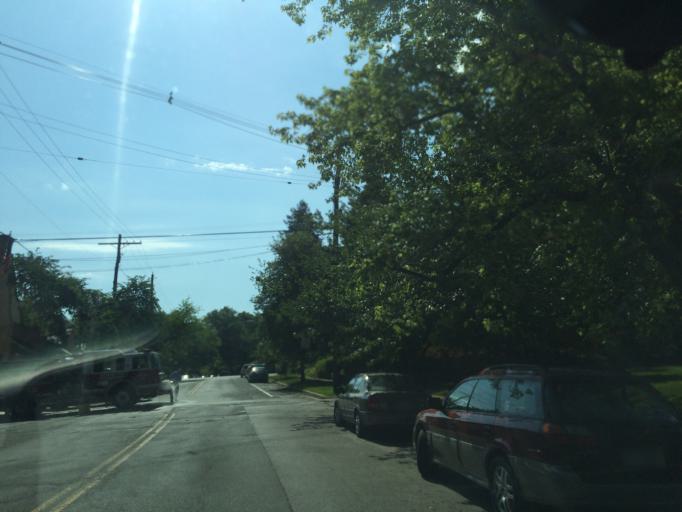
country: US
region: Maryland
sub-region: Baltimore County
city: Towson
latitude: 39.3503
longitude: -76.6365
